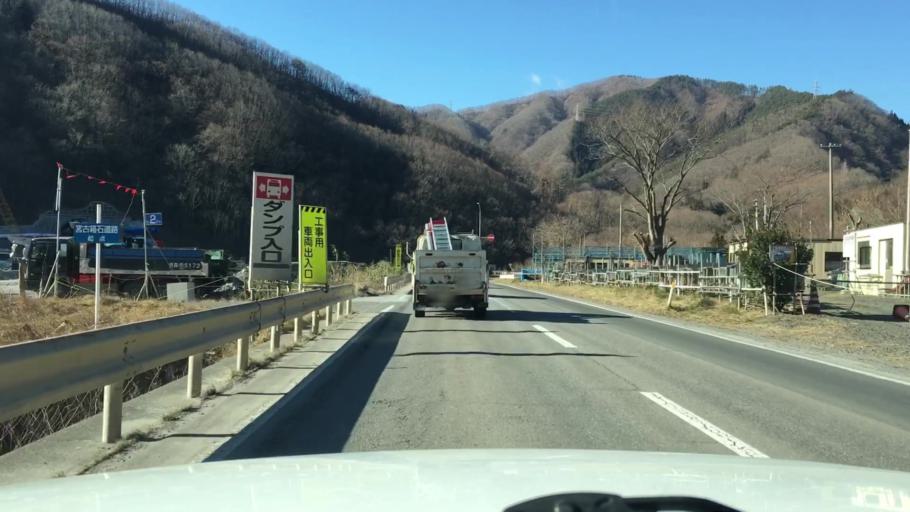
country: JP
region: Iwate
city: Miyako
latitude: 39.6235
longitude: 141.8249
